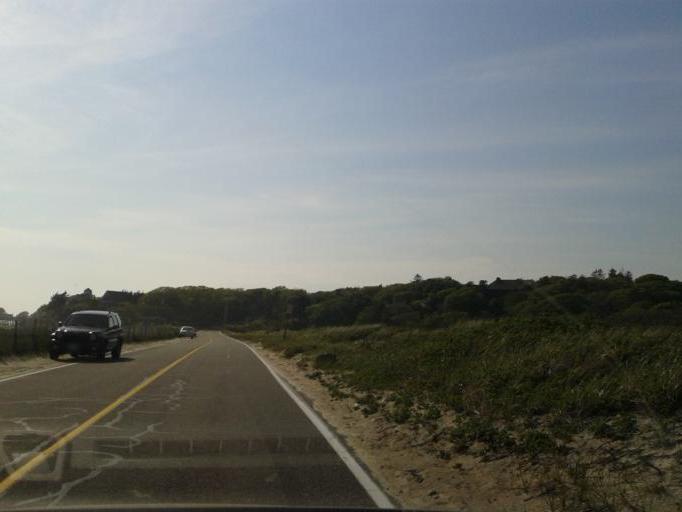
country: US
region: Massachusetts
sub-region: Barnstable County
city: Falmouth
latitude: 41.5173
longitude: -70.6583
